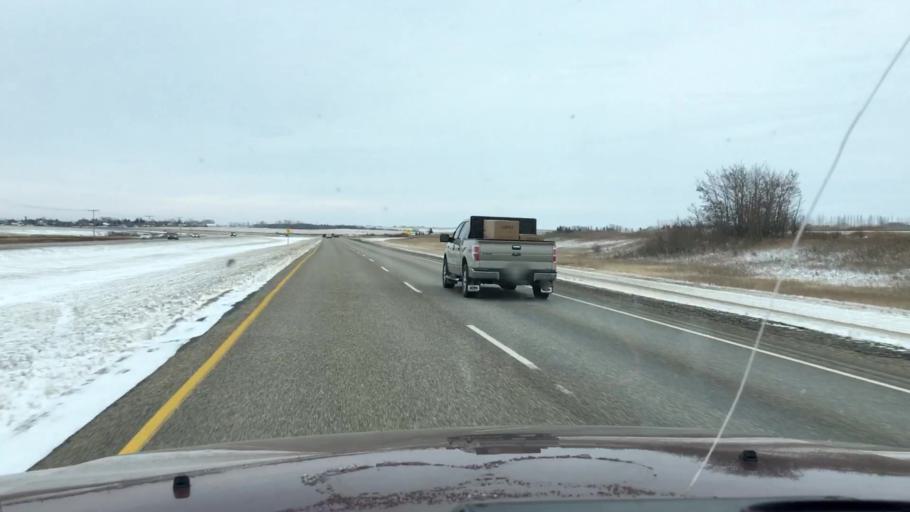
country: CA
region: Saskatchewan
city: Moose Jaw
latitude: 50.9535
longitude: -105.7095
